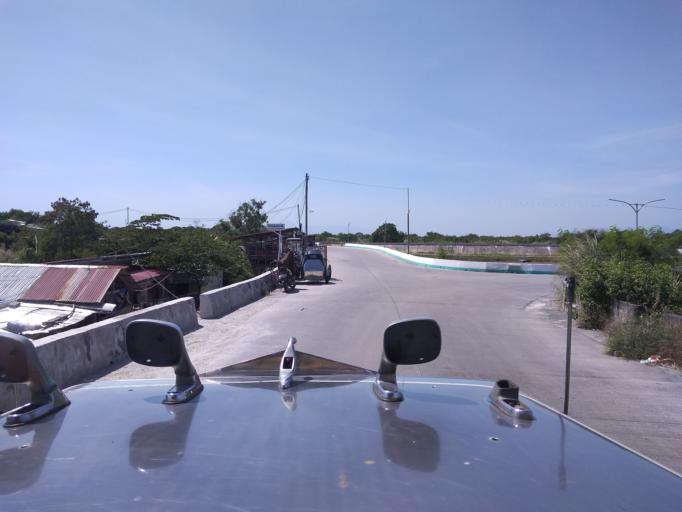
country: PH
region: Central Luzon
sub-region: Province of Pampanga
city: Minalin
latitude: 14.9665
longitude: 120.6637
